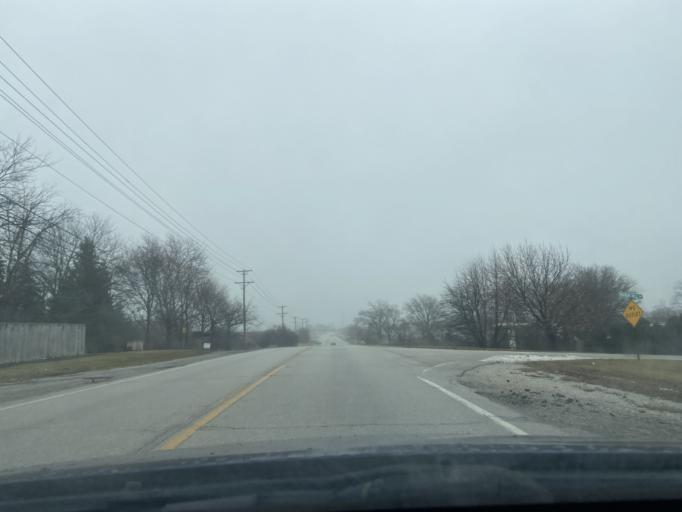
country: US
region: Illinois
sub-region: Lake County
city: Round Lake
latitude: 42.3142
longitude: -88.1035
